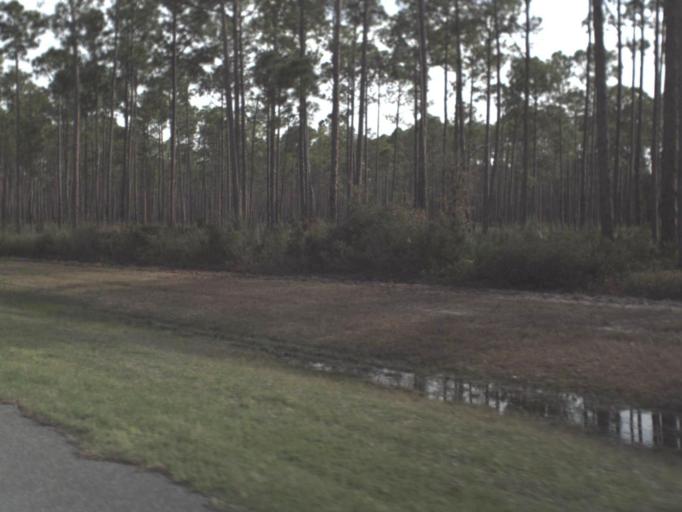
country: US
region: Florida
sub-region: Bay County
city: Mexico Beach
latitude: 29.9952
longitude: -85.4933
